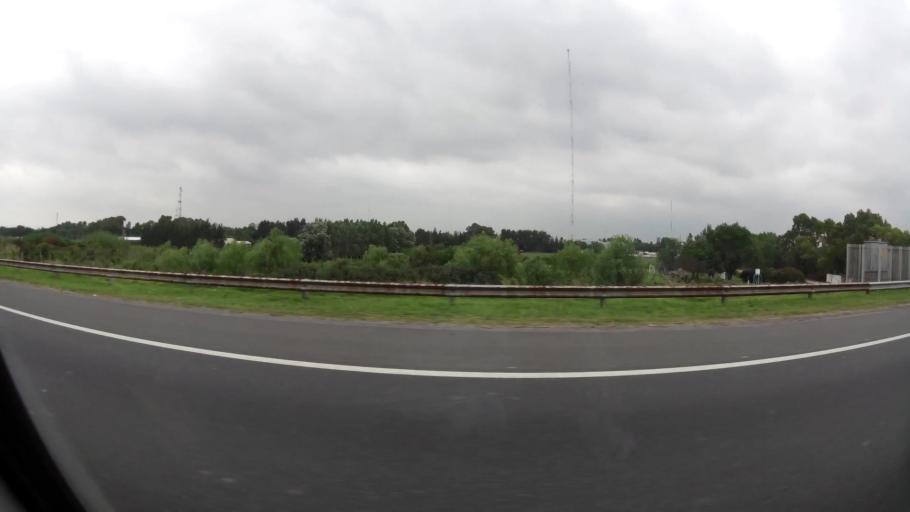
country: AR
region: Buenos Aires
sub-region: Partido de Avellaneda
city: Avellaneda
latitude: -34.6821
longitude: -58.3135
